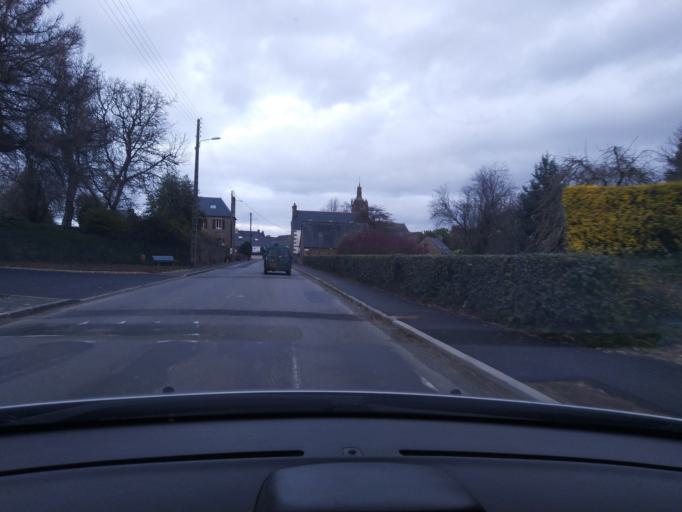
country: FR
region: Brittany
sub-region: Departement des Cotes-d'Armor
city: Plouaret
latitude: 48.6103
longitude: -3.4756
